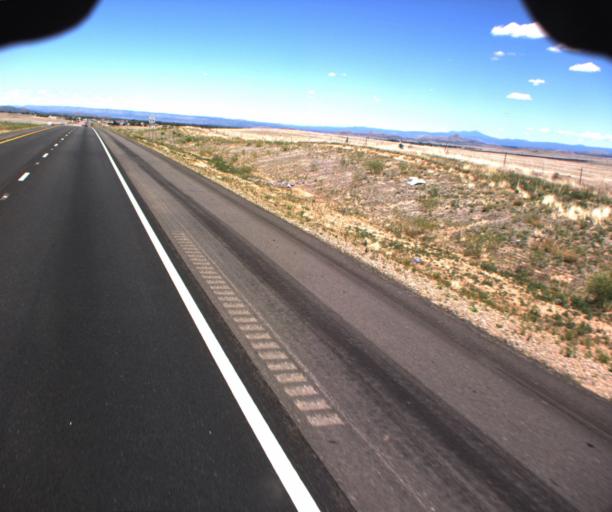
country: US
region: Arizona
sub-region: Yavapai County
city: Chino Valley
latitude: 34.6950
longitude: -112.4474
